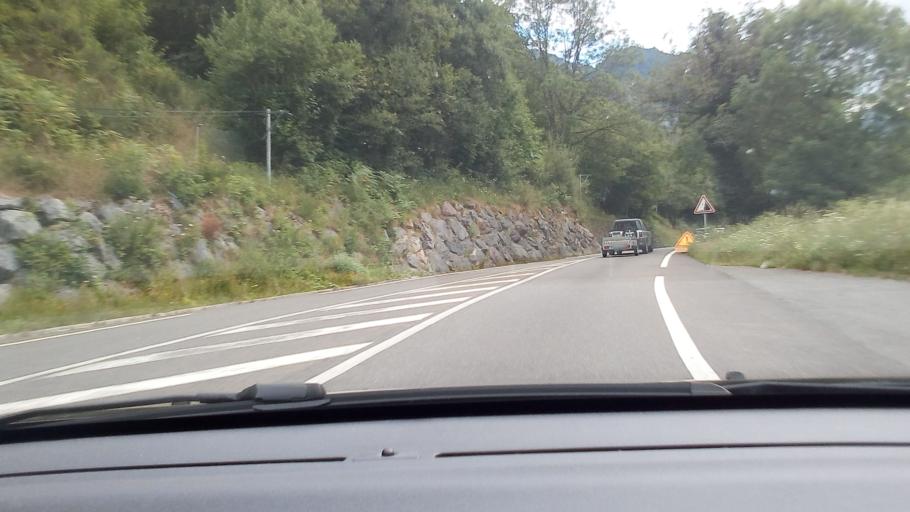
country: ES
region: Aragon
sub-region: Provincia de Huesca
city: Canfranc
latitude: 42.8593
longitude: -0.5488
